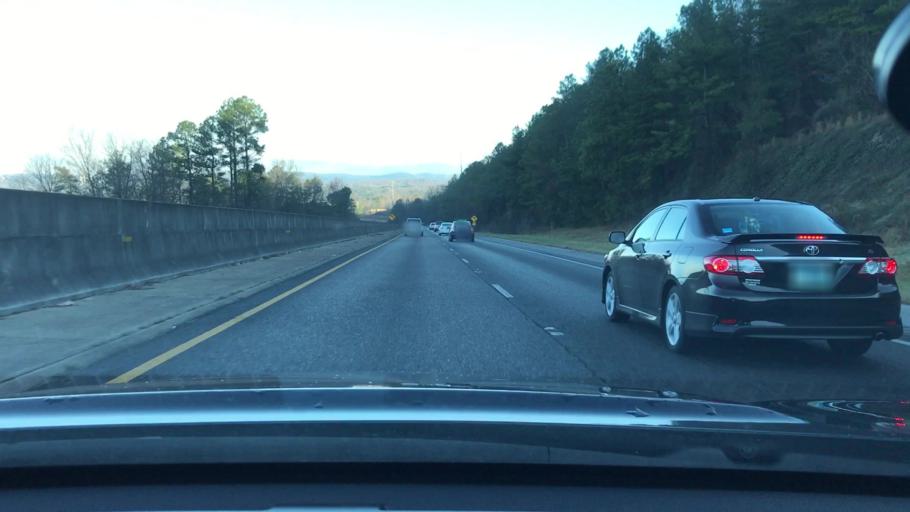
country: US
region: Alabama
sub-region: Shelby County
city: Meadowbrook
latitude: 33.3972
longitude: -86.6643
